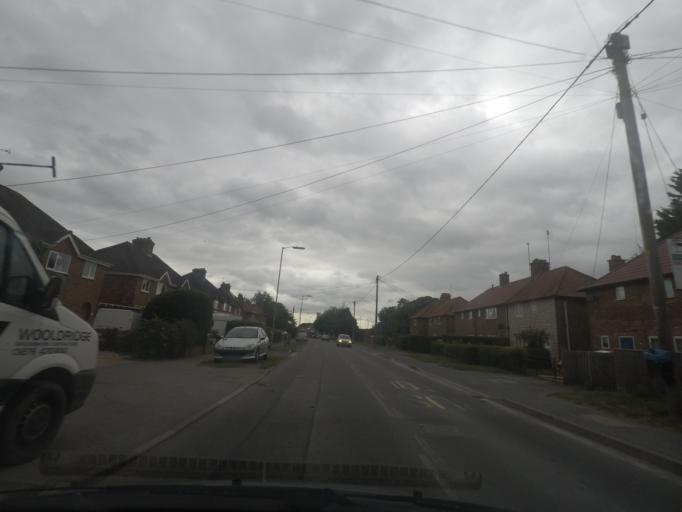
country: GB
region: England
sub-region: Oxfordshire
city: Didcot
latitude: 51.6072
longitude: -1.2523
